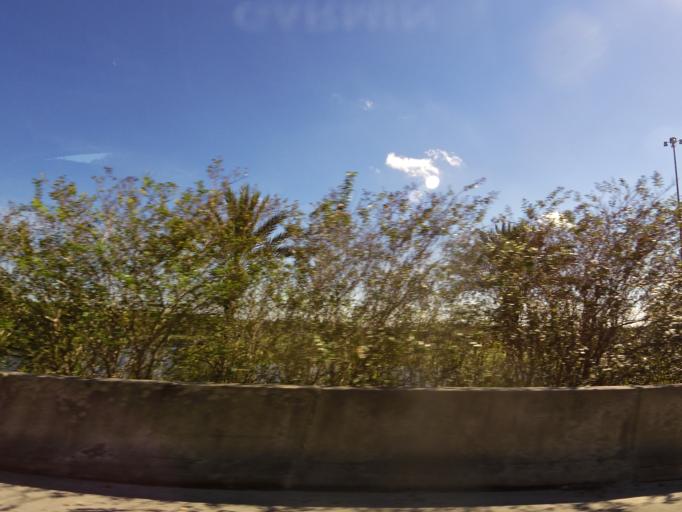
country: US
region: Florida
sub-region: Saint Johns County
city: Palm Valley
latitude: 30.1143
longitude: -81.4167
